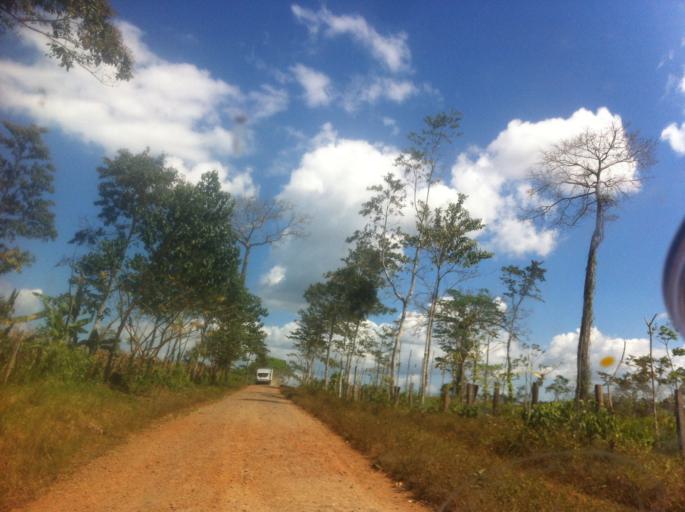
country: CR
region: Alajuela
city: Los Chiles
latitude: 11.2394
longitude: -84.4770
